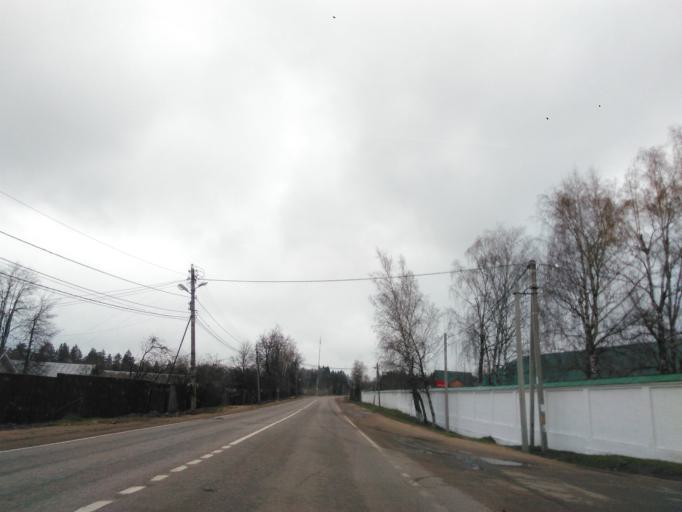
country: RU
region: Moskovskaya
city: Rozhdestveno
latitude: 55.8386
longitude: 37.0094
